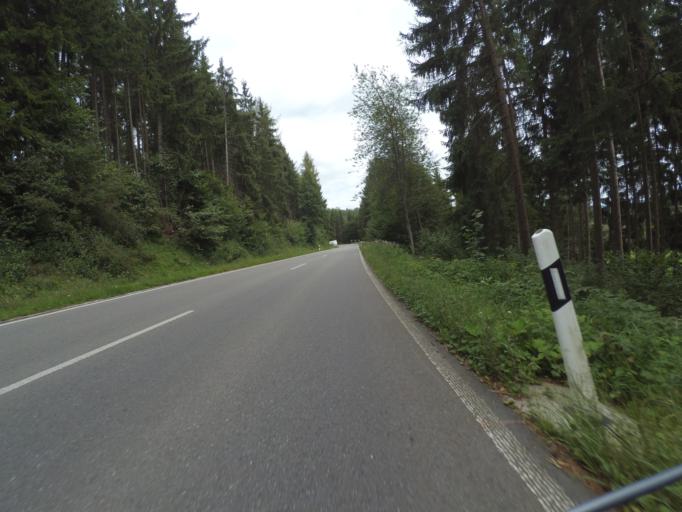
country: DE
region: Baden-Wuerttemberg
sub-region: Freiburg Region
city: Loffingen
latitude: 47.8935
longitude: 8.3541
